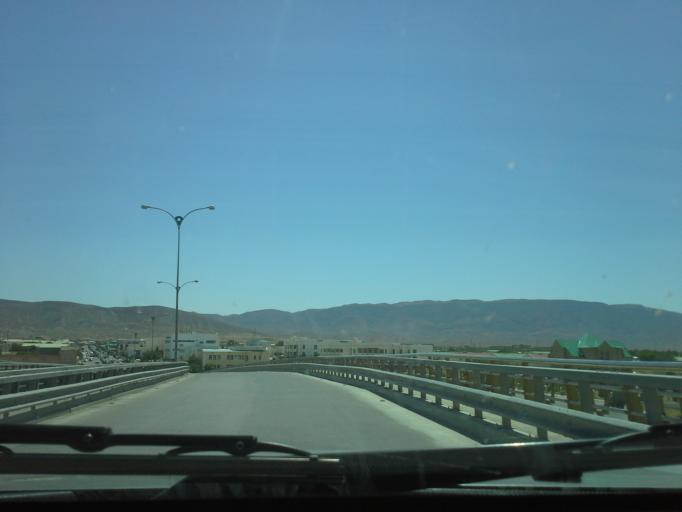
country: TM
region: Balkan
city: Serdar
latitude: 38.9792
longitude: 56.2780
